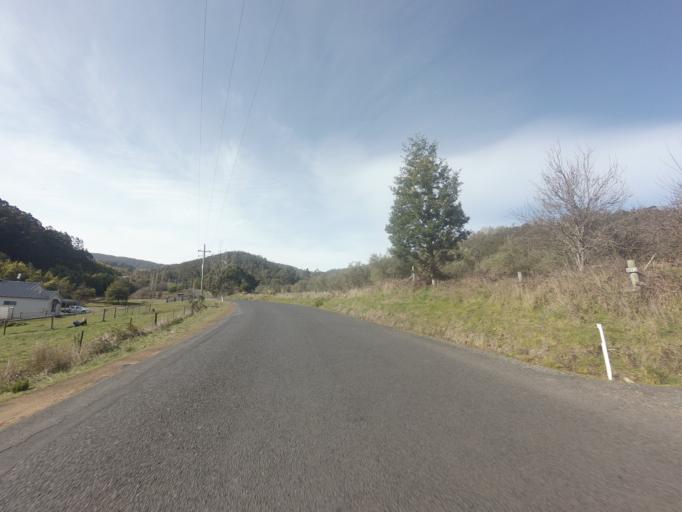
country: AU
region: Tasmania
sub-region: Huon Valley
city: Cygnet
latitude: -43.1792
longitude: 147.1417
